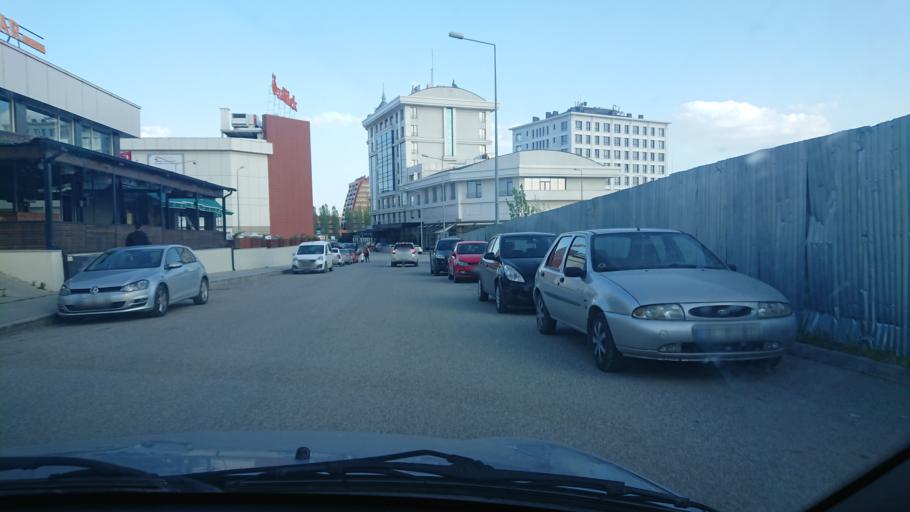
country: TR
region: Eskisehir
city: Eskisehir
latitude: 39.7846
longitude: 30.4960
